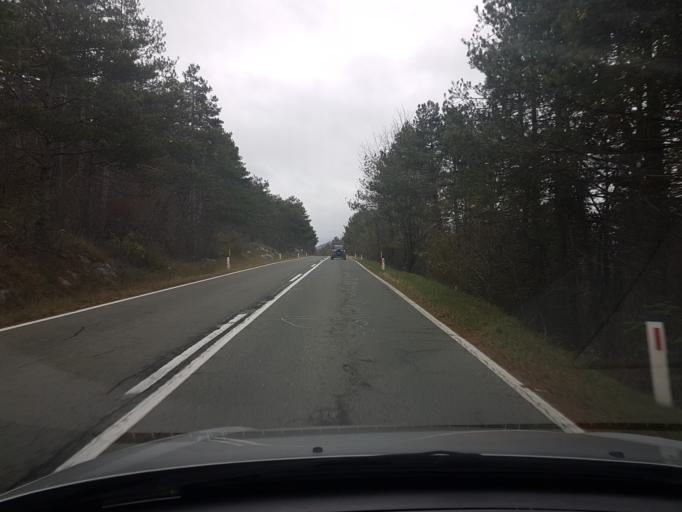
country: SI
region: Divaca
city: Divaca
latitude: 45.7267
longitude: 13.9745
